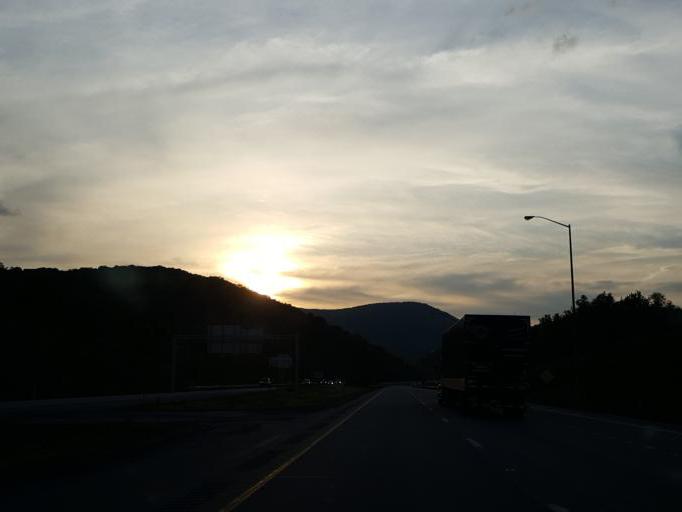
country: US
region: Pennsylvania
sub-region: Blair County
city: Duncansville
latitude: 40.4459
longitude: -78.4481
